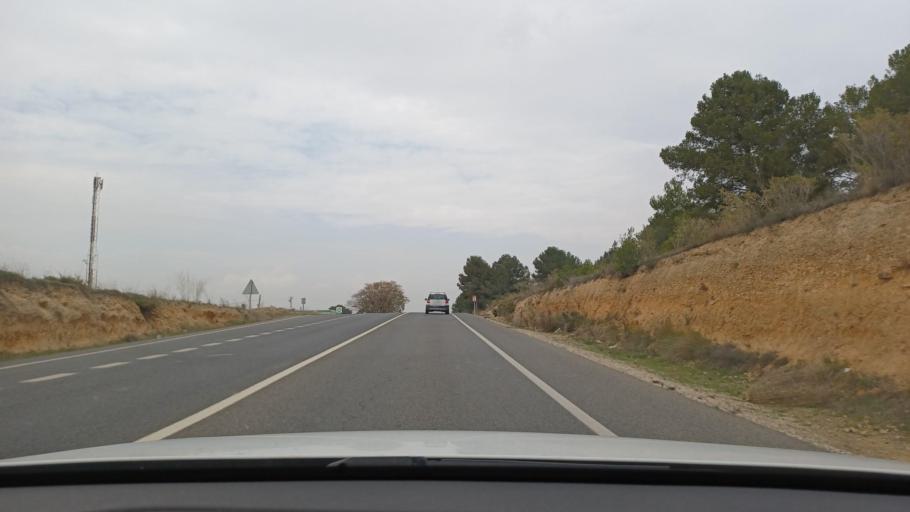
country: ES
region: Catalonia
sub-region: Provincia de Tarragona
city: la Pobla de Mafumet
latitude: 41.1718
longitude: 1.2396
